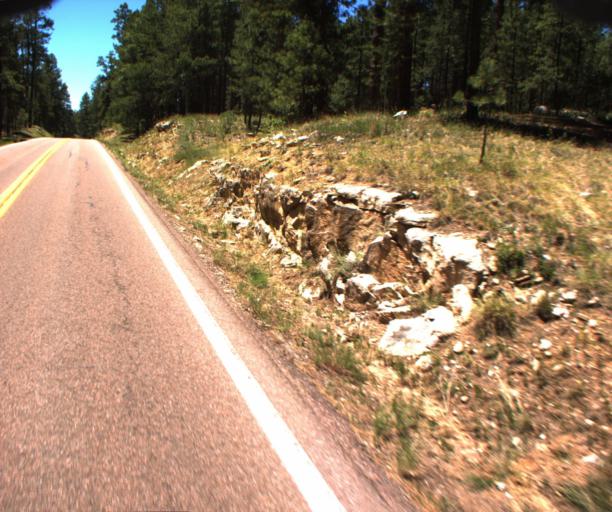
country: US
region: Arizona
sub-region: Gila County
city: Pine
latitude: 34.5439
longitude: -111.3241
